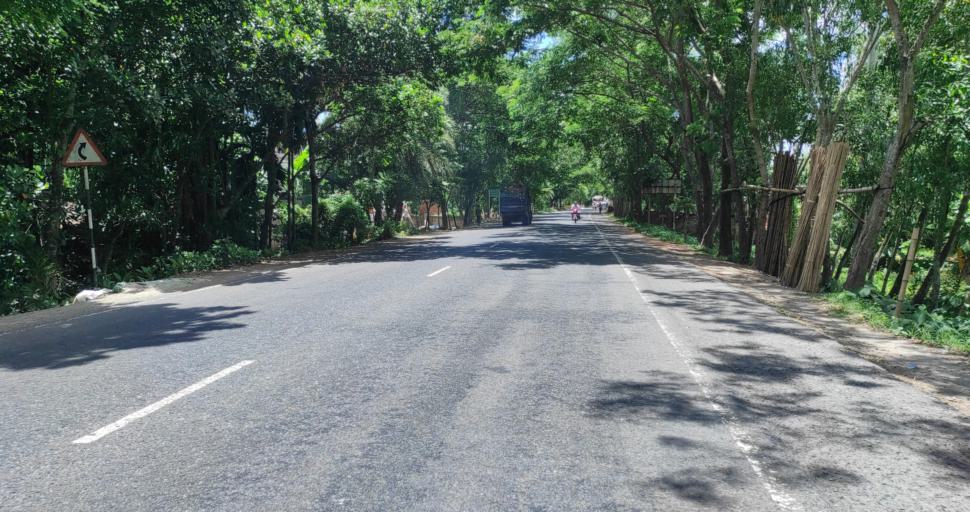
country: BD
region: Barisal
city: Gaurnadi
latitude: 22.8299
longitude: 90.2579
